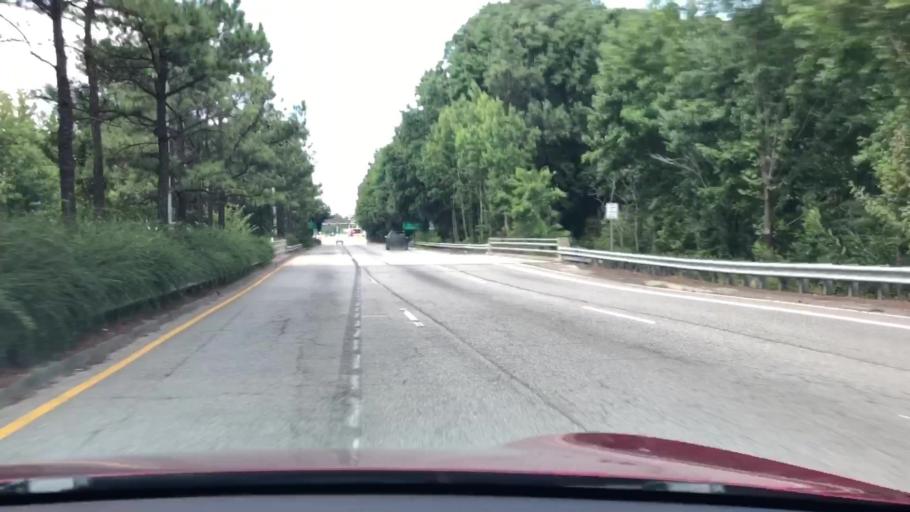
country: US
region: Virginia
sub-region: City of Norfolk
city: Norfolk
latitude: 36.8744
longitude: -76.2031
